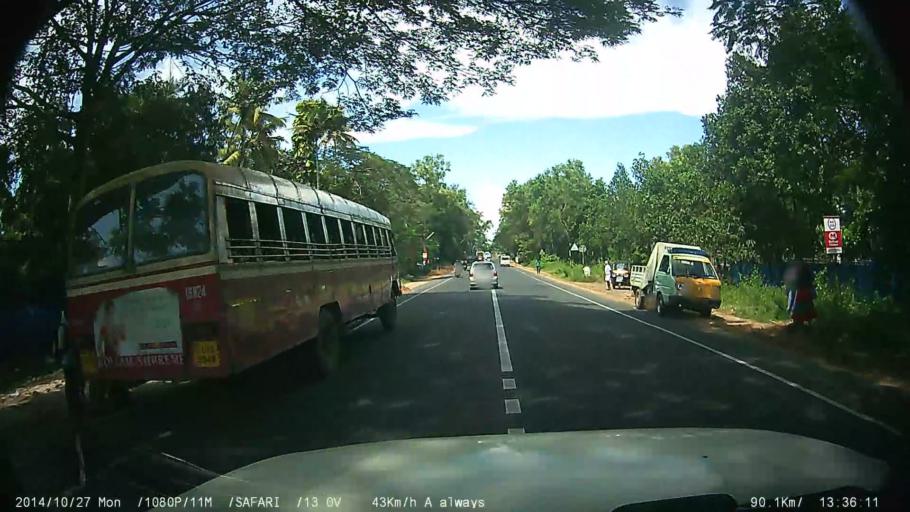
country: IN
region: Kerala
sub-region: Alappuzha
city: Shertallai
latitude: 9.6007
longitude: 76.3283
